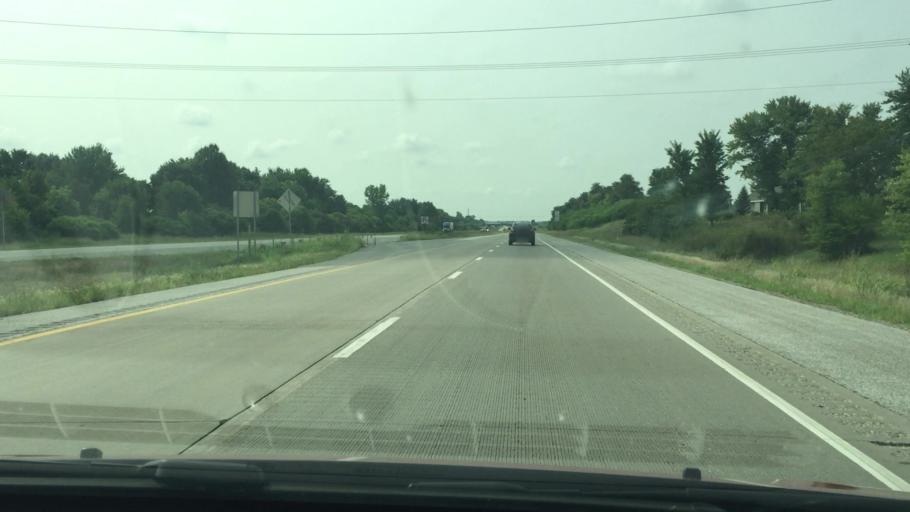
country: US
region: Iowa
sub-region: Scott County
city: Walcott
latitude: 41.5826
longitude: -90.6765
